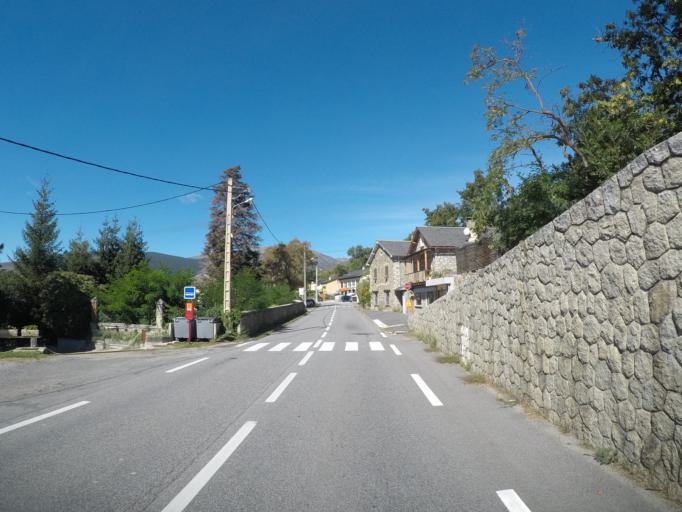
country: ES
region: Catalonia
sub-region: Provincia de Girona
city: Puigcerda
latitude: 42.4589
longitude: 1.9198
